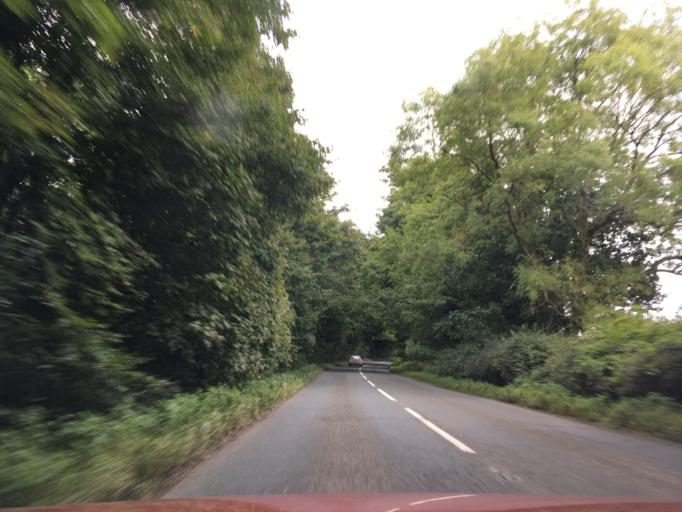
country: GB
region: England
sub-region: Gloucestershire
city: Wotton-under-Edge
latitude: 51.6599
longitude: -2.3218
